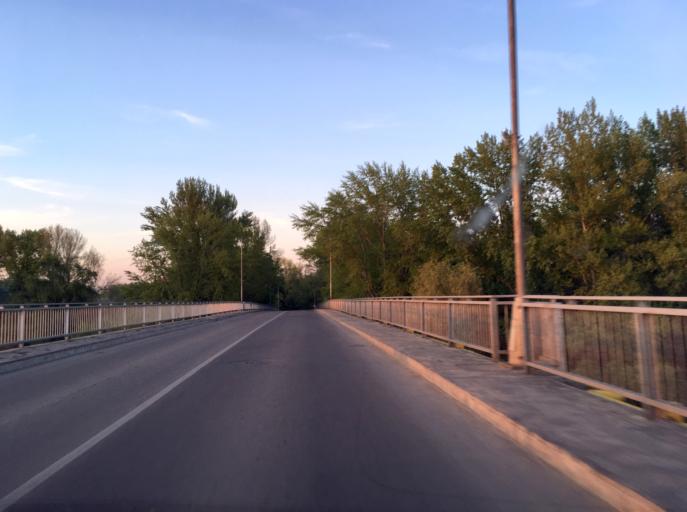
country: SK
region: Nitriansky
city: Kolarovo
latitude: 47.9141
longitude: 18.0104
